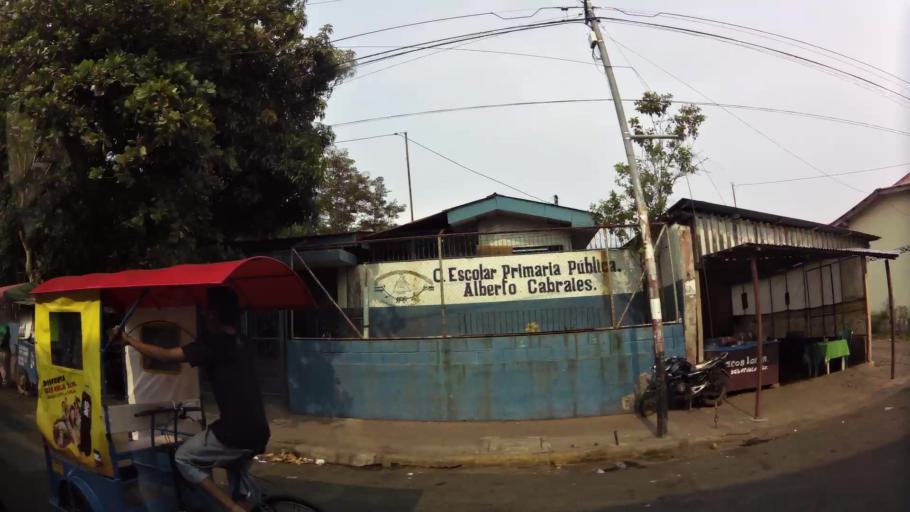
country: NI
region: Chinandega
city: Chinandega
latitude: 12.6284
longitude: -87.1324
